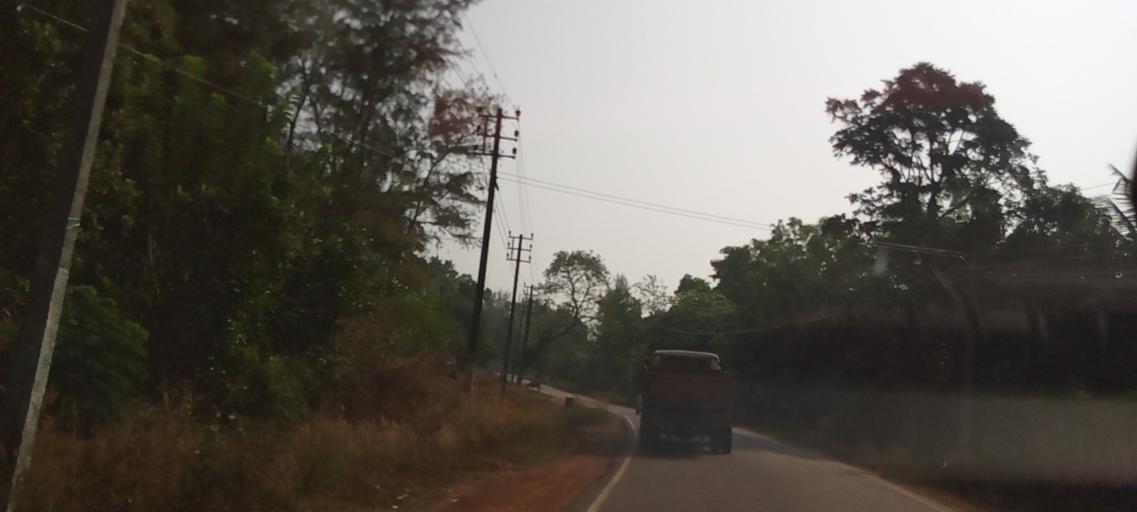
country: IN
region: Karnataka
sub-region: Udupi
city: Coondapoor
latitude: 13.5136
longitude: 74.7398
